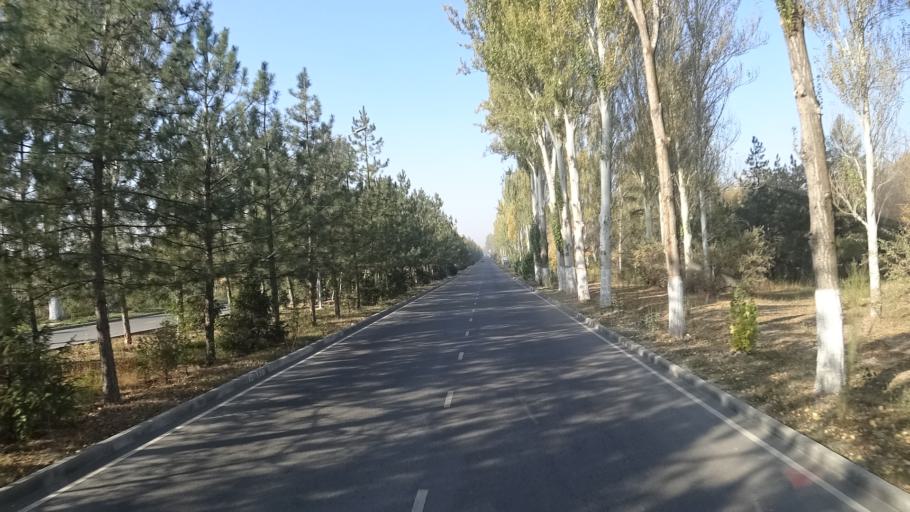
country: KG
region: Chuy
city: Bishkek
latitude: 43.0508
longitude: 74.4506
